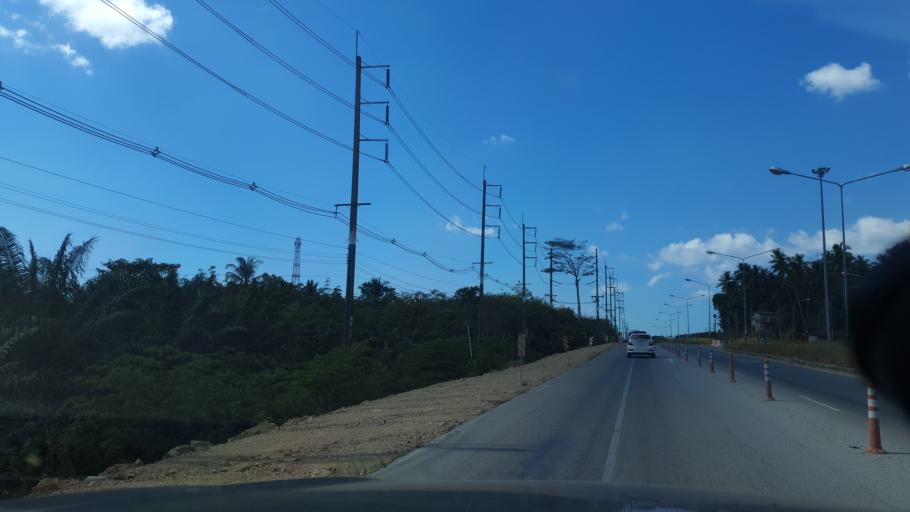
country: TH
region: Phangnga
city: Ban Khao Lak
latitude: 8.5355
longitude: 98.2820
